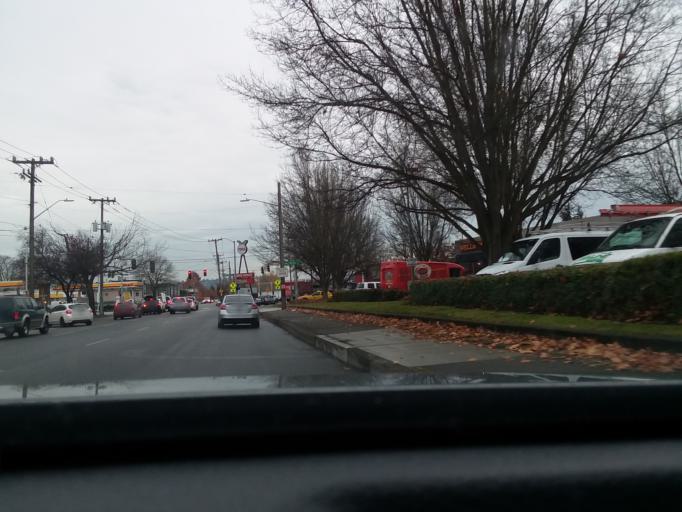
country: US
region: Washington
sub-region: King County
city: White Center
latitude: 47.5485
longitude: -122.3213
